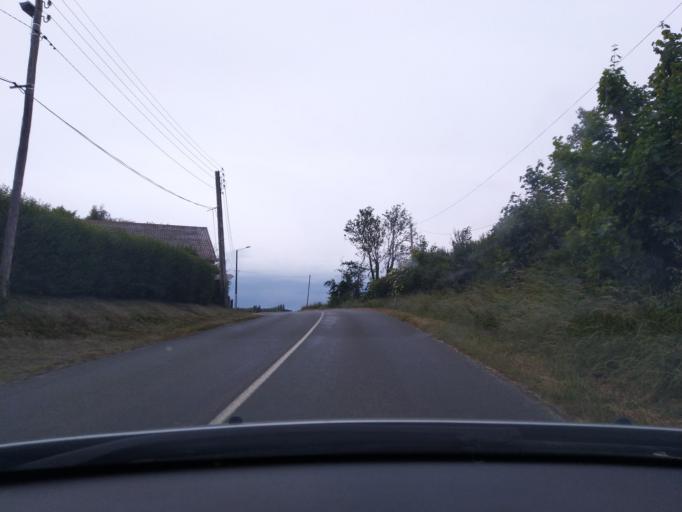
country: FR
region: Nord-Pas-de-Calais
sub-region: Departement du Pas-de-Calais
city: Wissant
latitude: 50.8569
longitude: 1.6756
